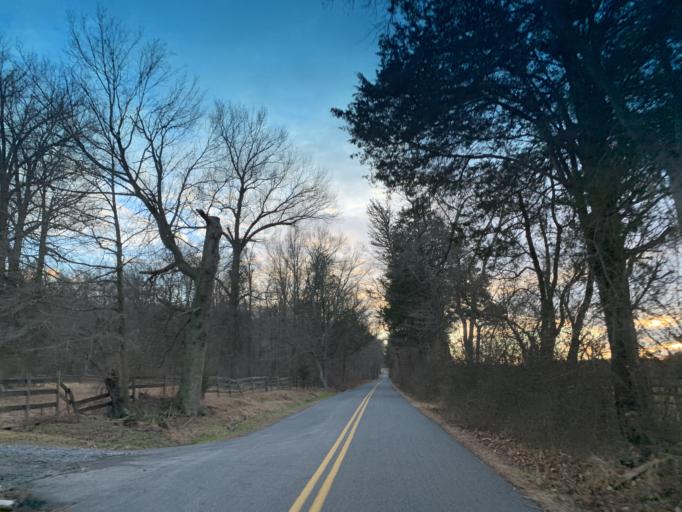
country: US
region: Maryland
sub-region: Harford County
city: Bel Air North
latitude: 39.6133
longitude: -76.3166
